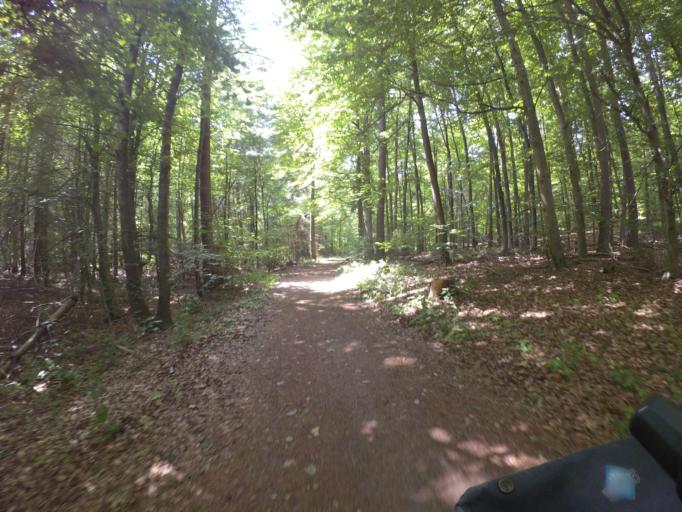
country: DE
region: Rheinland-Pfalz
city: Rodenbach
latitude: 49.4651
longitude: 7.6789
